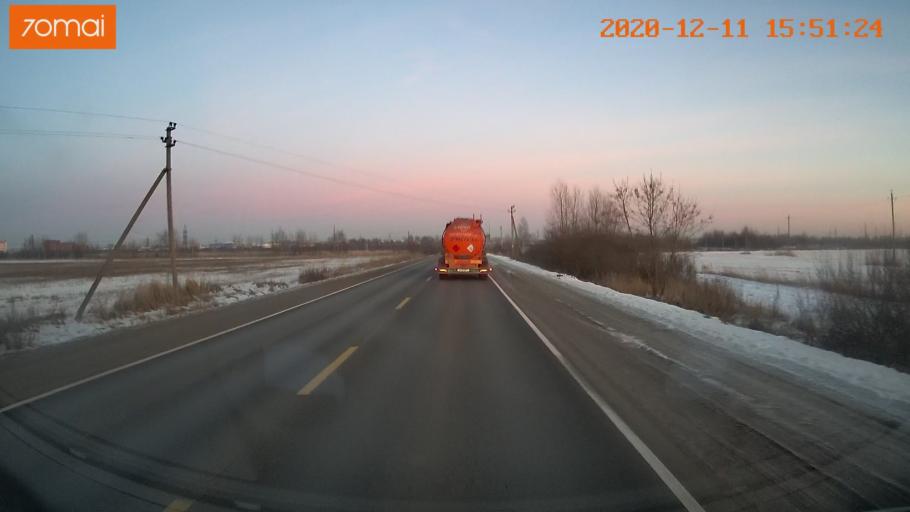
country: RU
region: Ivanovo
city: Novo-Talitsy
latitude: 56.9868
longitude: 40.8967
